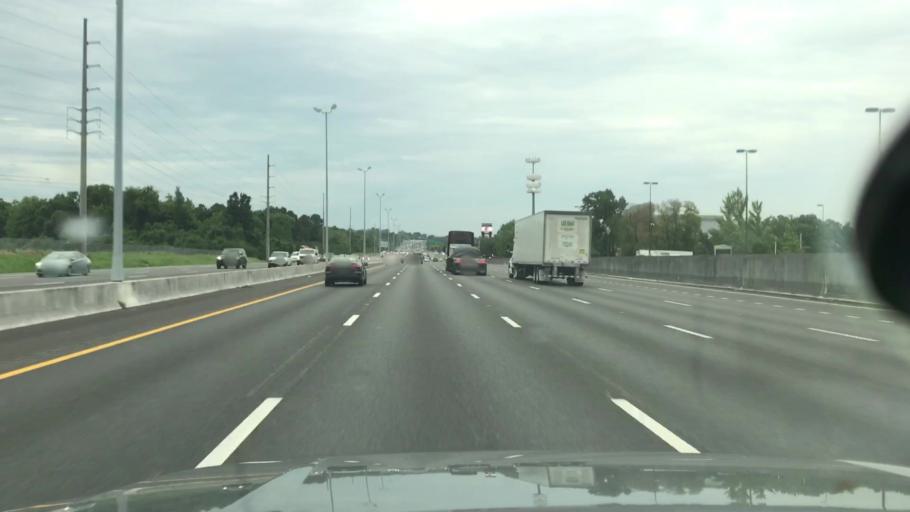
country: US
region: Tennessee
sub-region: Davidson County
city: Lakewood
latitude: 36.2117
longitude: -86.6915
